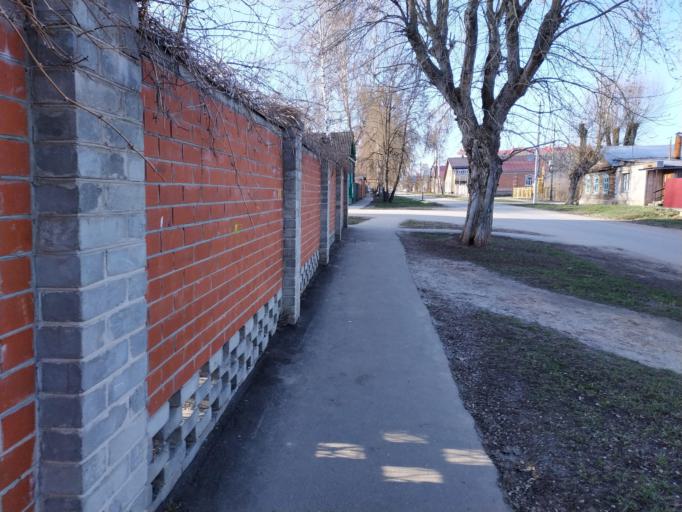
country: RU
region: Nizjnij Novgorod
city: Arzamas
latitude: 55.3970
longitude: 43.8147
